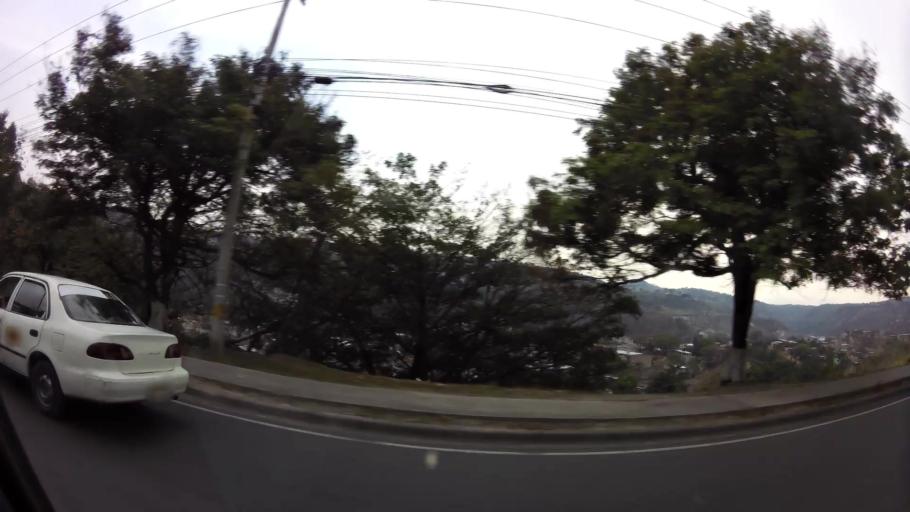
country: HN
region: Francisco Morazan
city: Tegucigalpa
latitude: 14.0886
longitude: -87.2369
